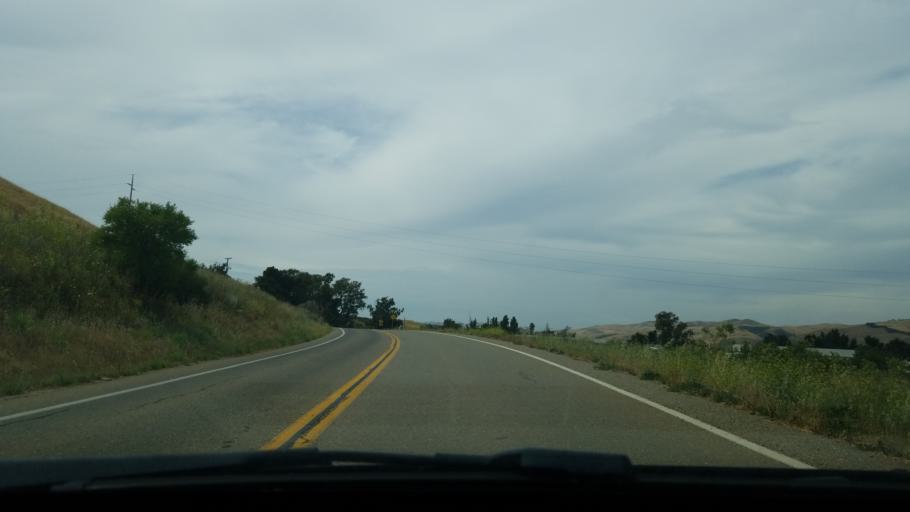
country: US
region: California
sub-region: Santa Barbara County
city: Orcutt
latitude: 34.8807
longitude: -120.3133
